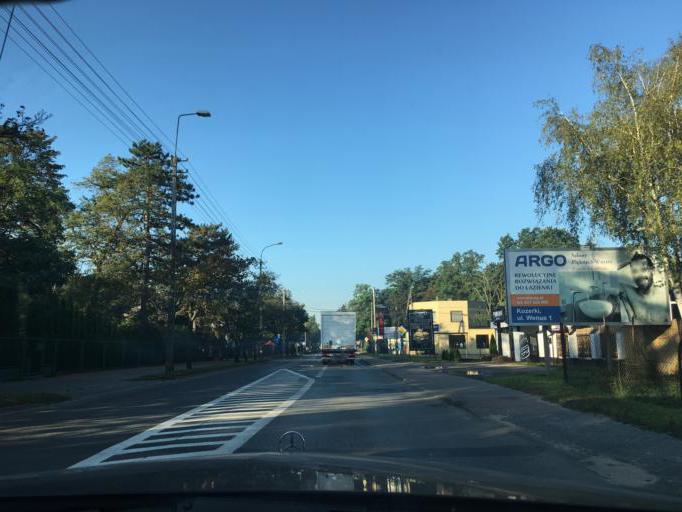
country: PL
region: Masovian Voivodeship
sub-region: Powiat grodziski
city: Milanowek
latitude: 52.1210
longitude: 20.6782
